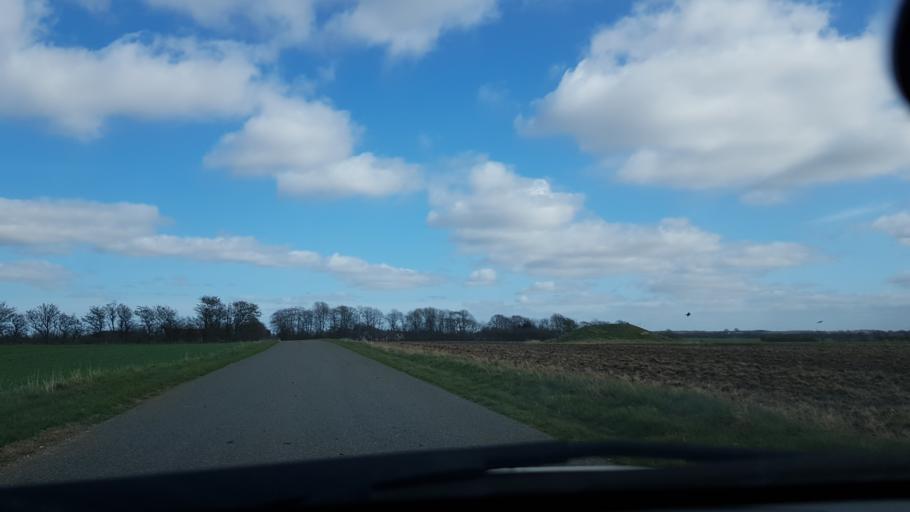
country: DK
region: South Denmark
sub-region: Vejen Kommune
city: Rodding
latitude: 55.3731
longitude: 8.9807
